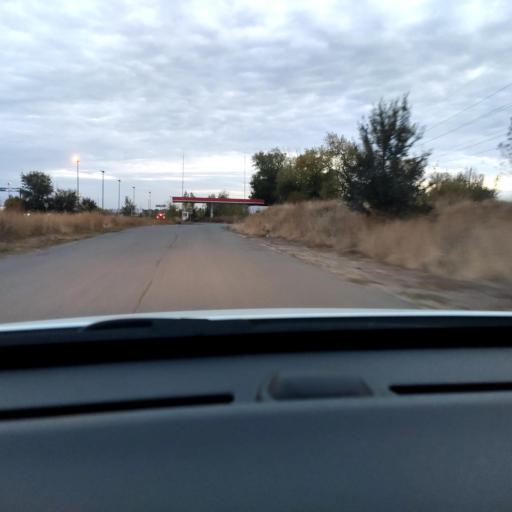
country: RU
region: Voronezj
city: Somovo
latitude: 51.6580
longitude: 39.3016
